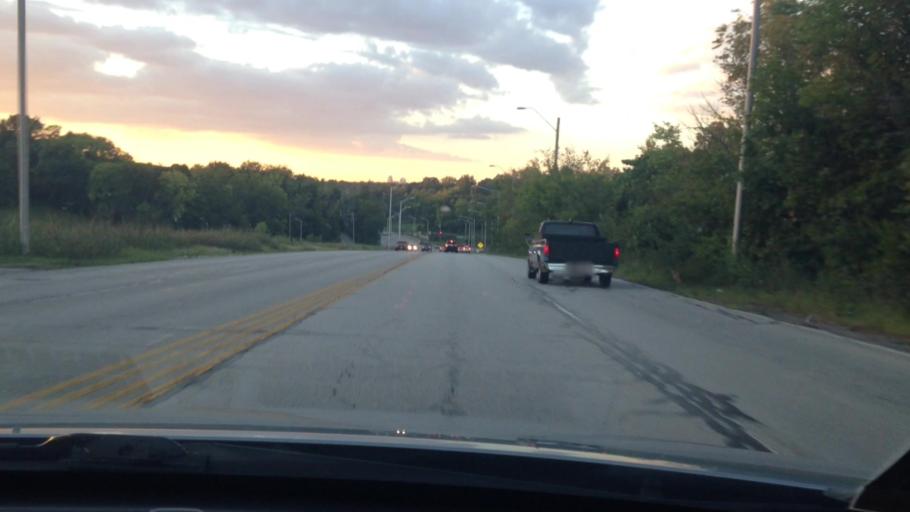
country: US
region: Missouri
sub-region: Jackson County
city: Raytown
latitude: 39.0268
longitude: -94.5062
